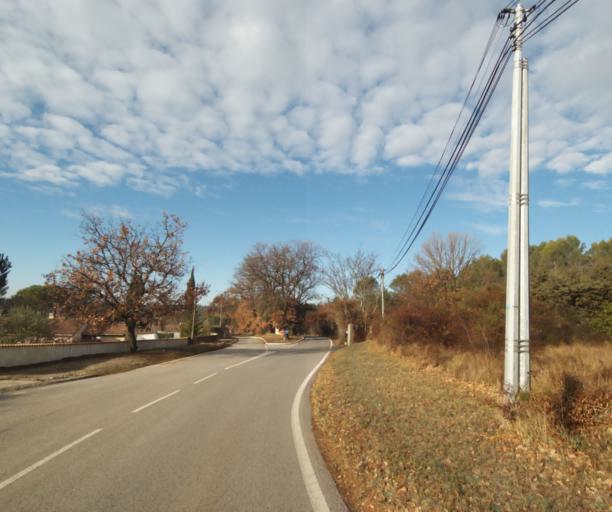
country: FR
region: Provence-Alpes-Cote d'Azur
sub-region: Departement du Var
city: Trans-en-Provence
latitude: 43.4908
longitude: 6.4807
